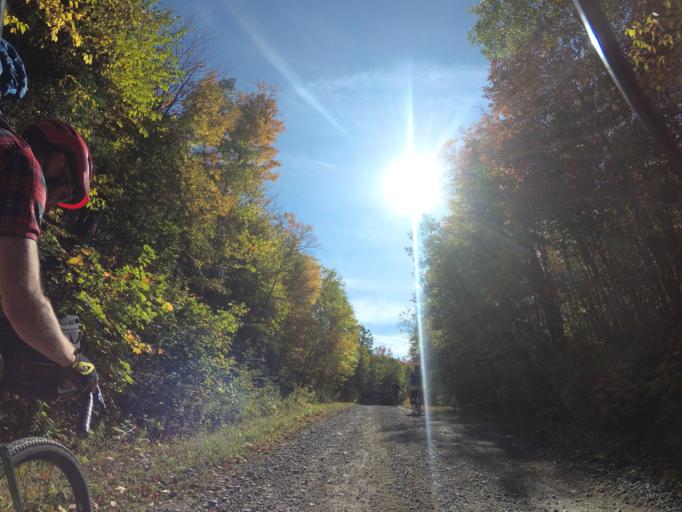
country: CA
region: Ontario
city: Renfrew
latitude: 45.3455
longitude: -77.0866
